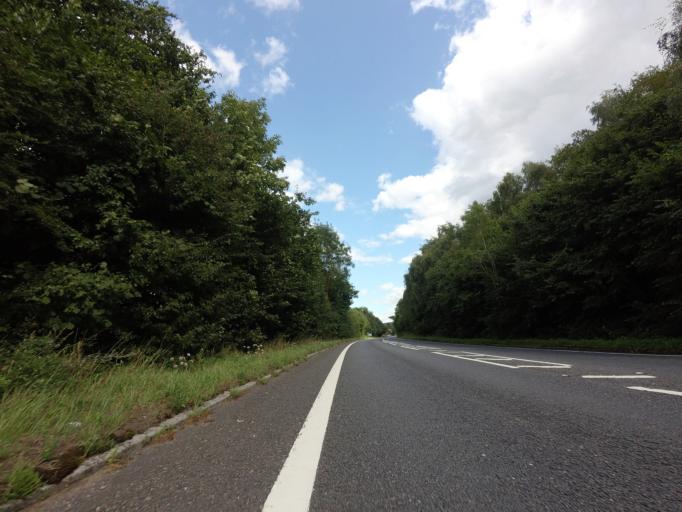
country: GB
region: England
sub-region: Kent
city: Borough Green
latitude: 51.2920
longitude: 0.2880
